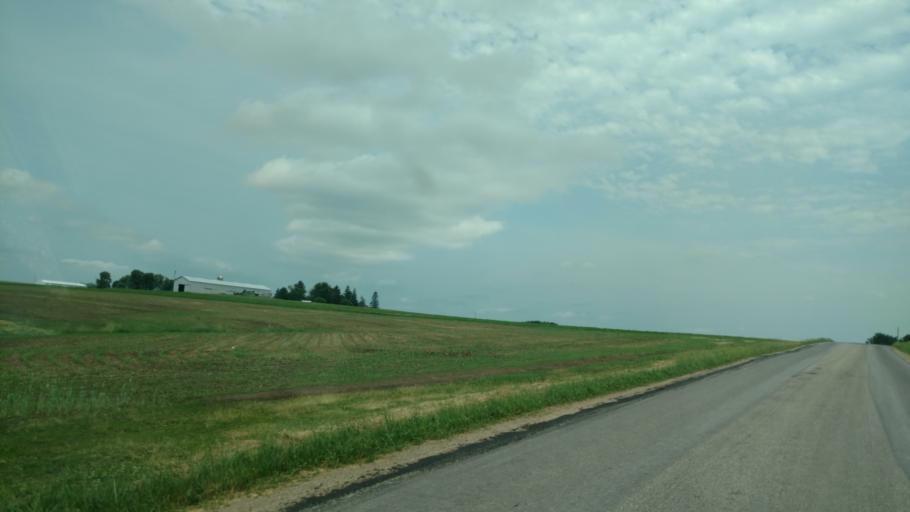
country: US
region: Wisconsin
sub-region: Monroe County
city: Cashton
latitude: 43.7113
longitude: -90.7103
